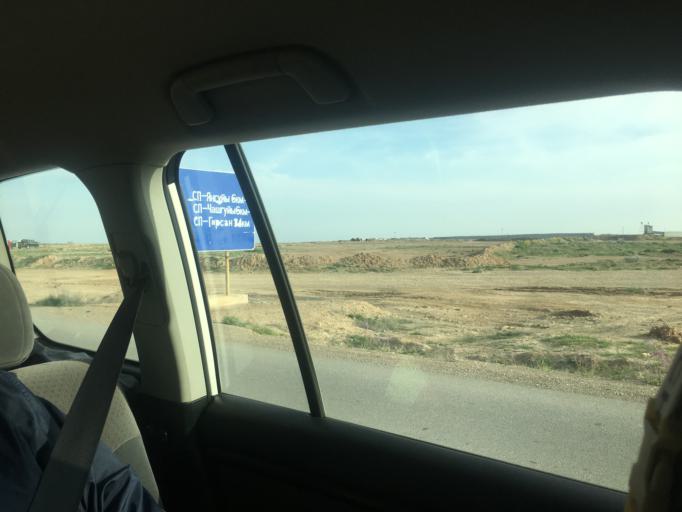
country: UZ
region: Qashqadaryo
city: Yangi Mirishkor
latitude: 38.5760
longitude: 64.7834
